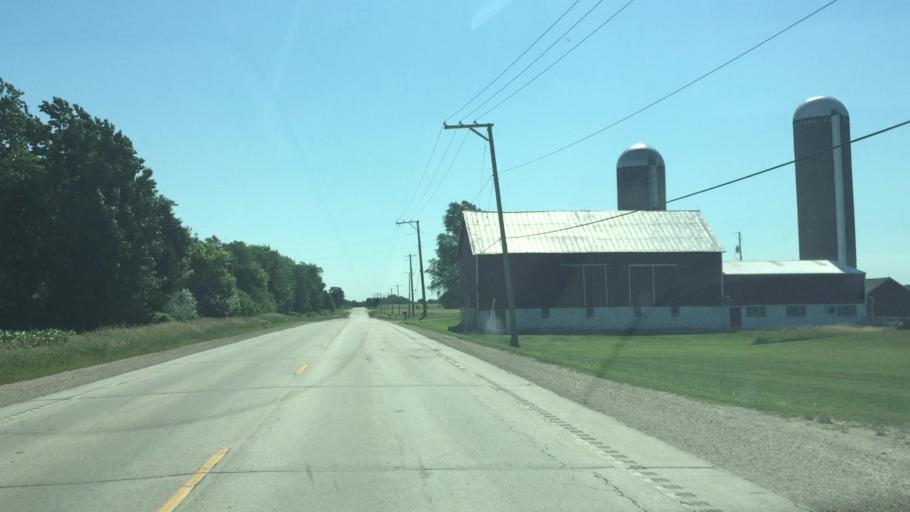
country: US
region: Wisconsin
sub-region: Calumet County
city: Hilbert
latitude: 44.1402
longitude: -88.1926
